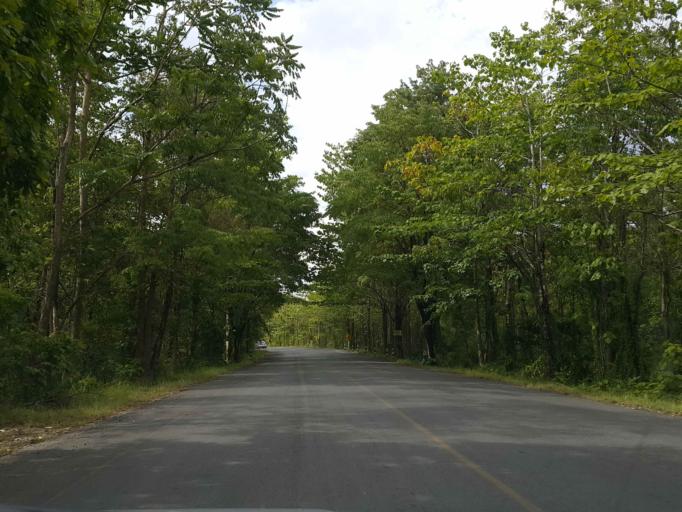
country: TH
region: Sukhothai
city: Thung Saliam
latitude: 17.4430
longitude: 99.3719
